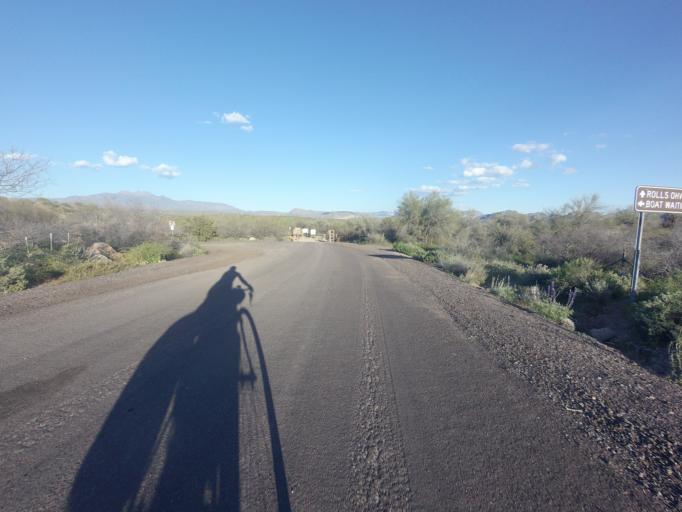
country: US
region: Arizona
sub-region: Maricopa County
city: Fountain Hills
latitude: 33.5936
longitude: -111.5428
